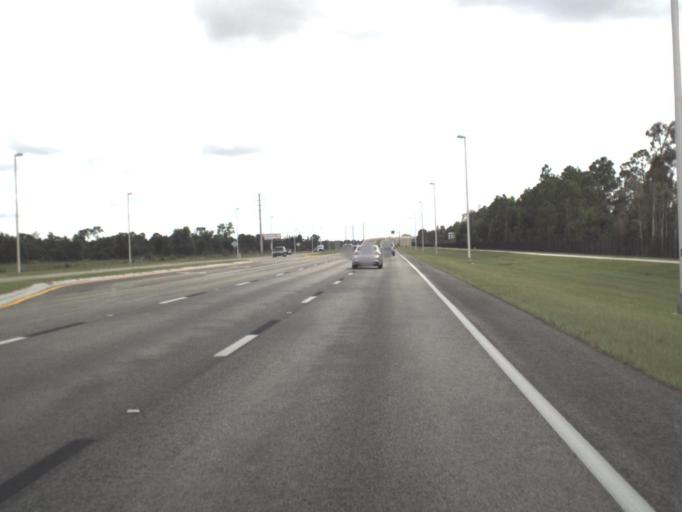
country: US
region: Florida
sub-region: Lee County
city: Villas
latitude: 26.5050
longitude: -81.8493
